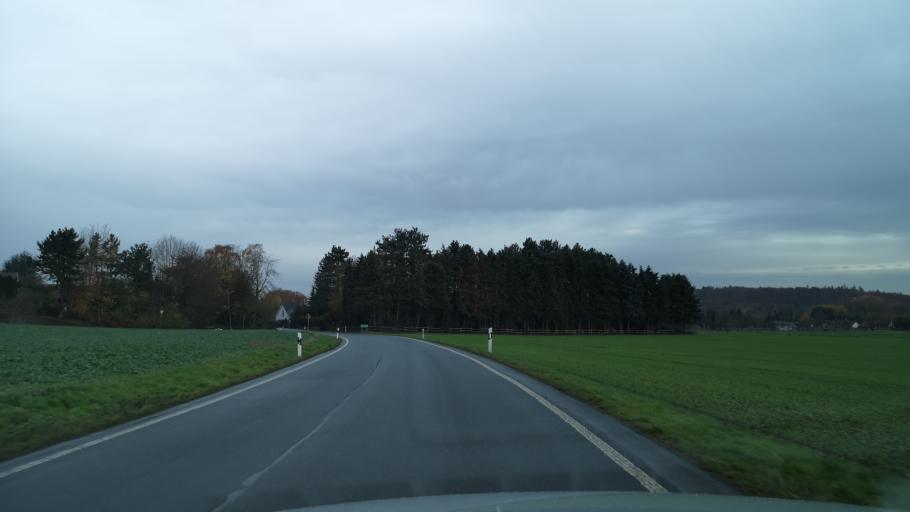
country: DE
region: North Rhine-Westphalia
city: Wickede
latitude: 51.4482
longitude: 7.8595
